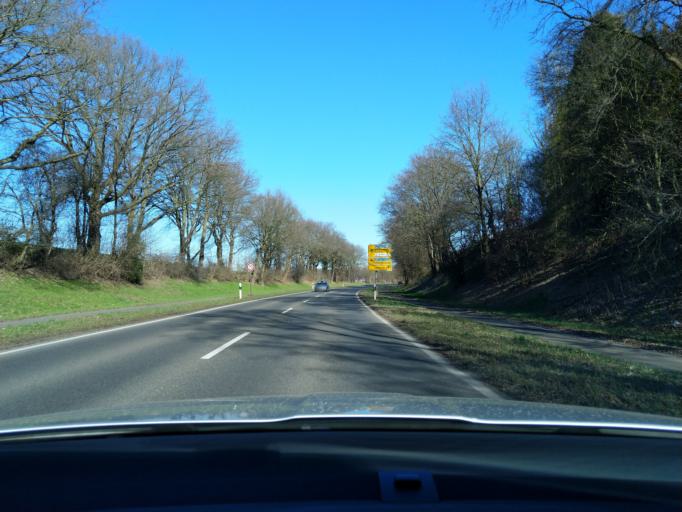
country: DE
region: North Rhine-Westphalia
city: Wegberg
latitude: 51.1471
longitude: 6.2682
